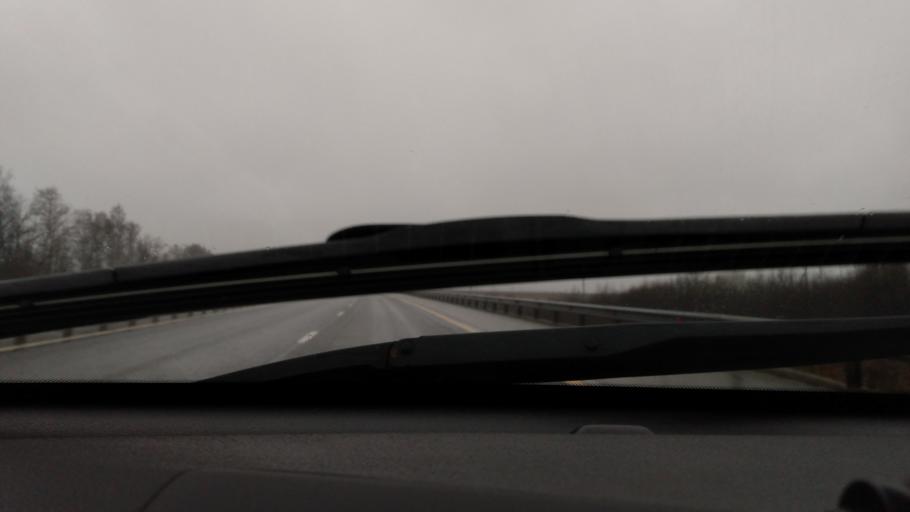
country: RU
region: Tula
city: Gritsovskiy
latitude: 54.2348
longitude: 38.1261
